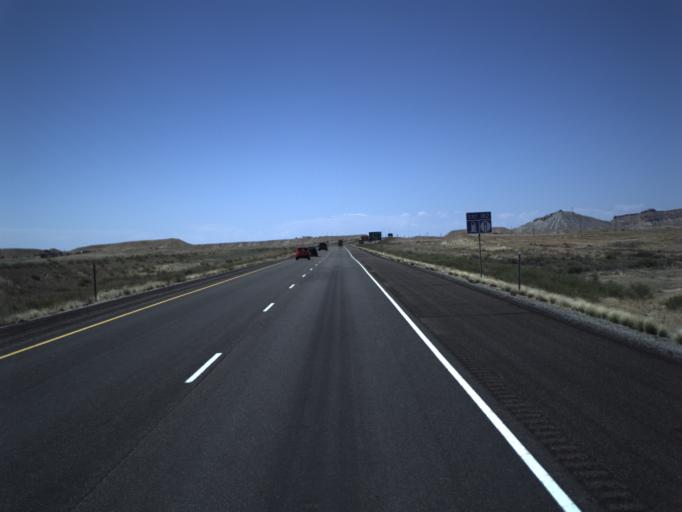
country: US
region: Utah
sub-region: Grand County
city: Moab
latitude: 38.9462
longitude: -109.7961
